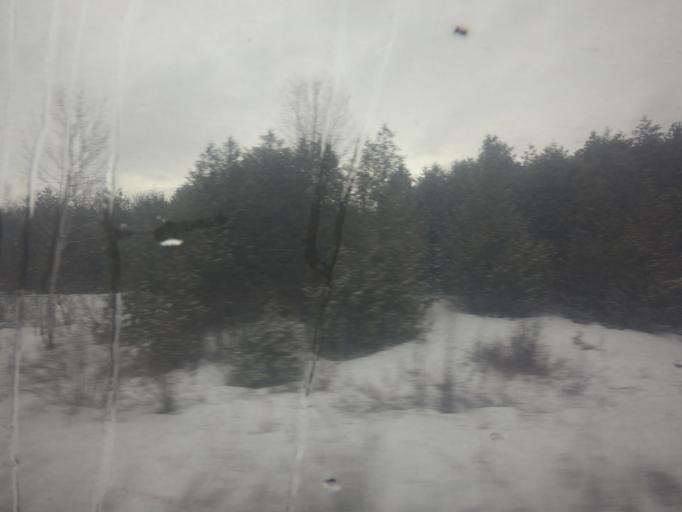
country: CA
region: Ontario
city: Bells Corners
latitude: 45.1705
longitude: -75.8328
